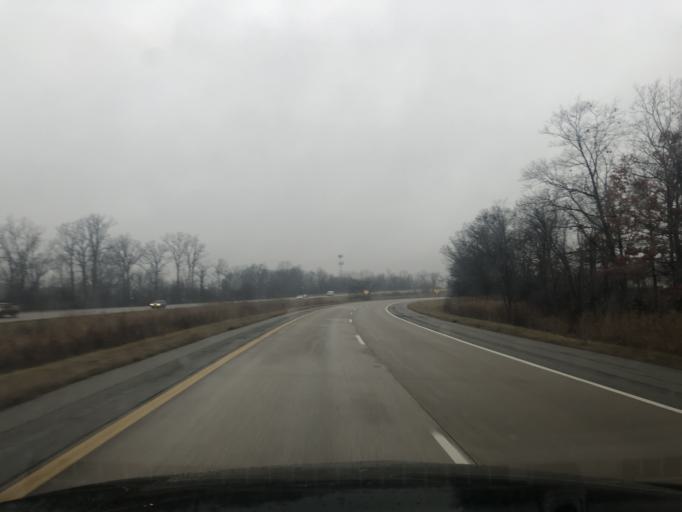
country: US
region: Michigan
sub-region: Wayne County
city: Taylor
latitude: 42.1903
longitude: -83.2603
